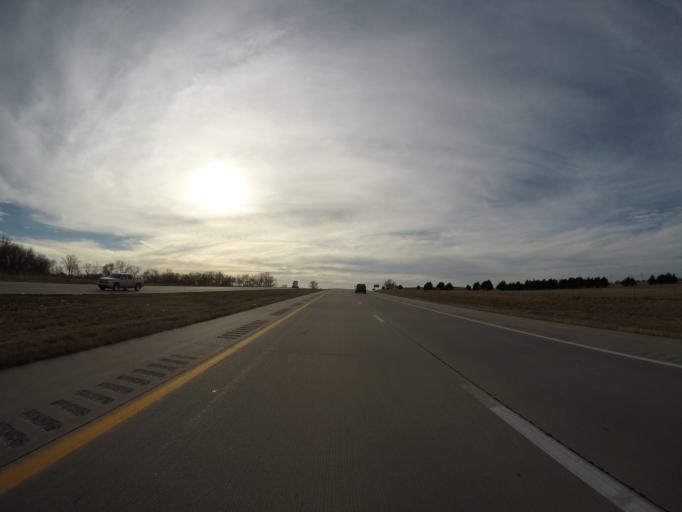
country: US
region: Kansas
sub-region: Franklin County
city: Wellsville
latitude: 38.7079
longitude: -95.0632
